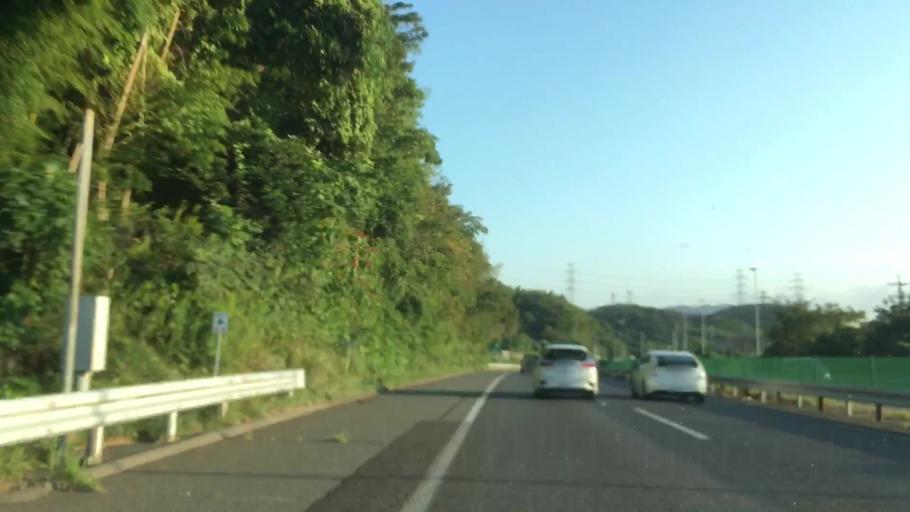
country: JP
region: Yamaguchi
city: Shimonoseki
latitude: 33.9833
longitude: 130.9520
